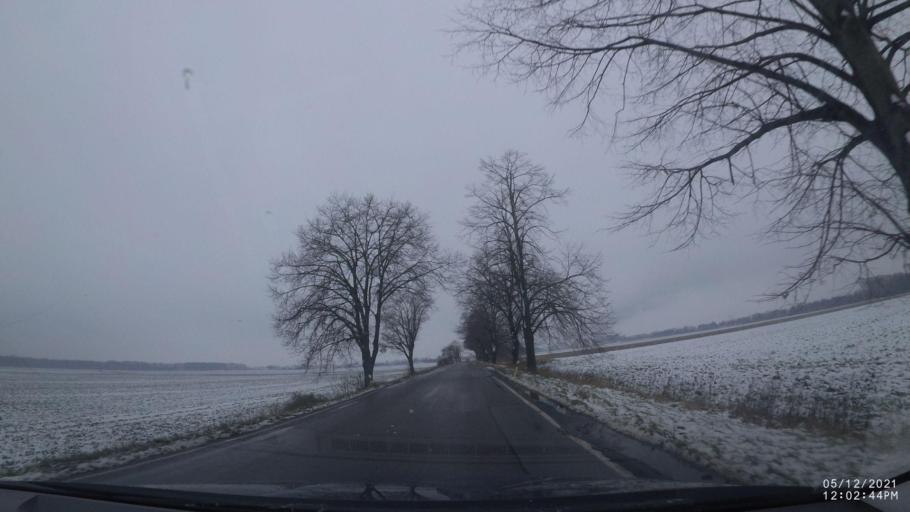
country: CZ
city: Ceske Mezirici
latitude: 50.2797
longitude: 16.0730
